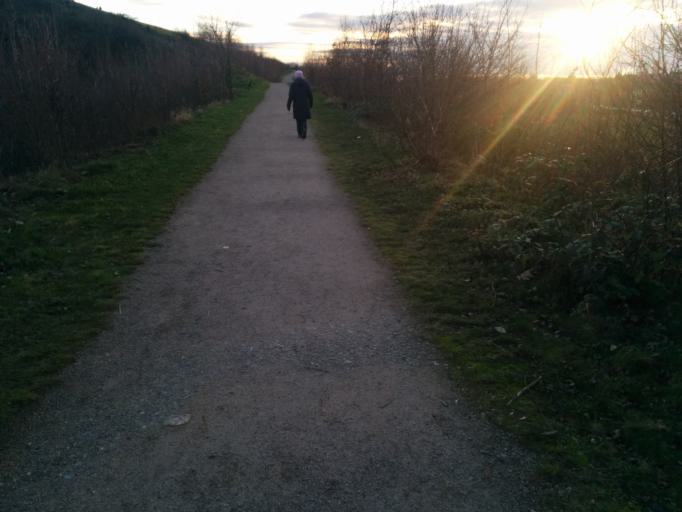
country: DE
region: North Rhine-Westphalia
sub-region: Regierungsbezirk Dusseldorf
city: Hochfeld
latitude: 51.3773
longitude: 6.7378
